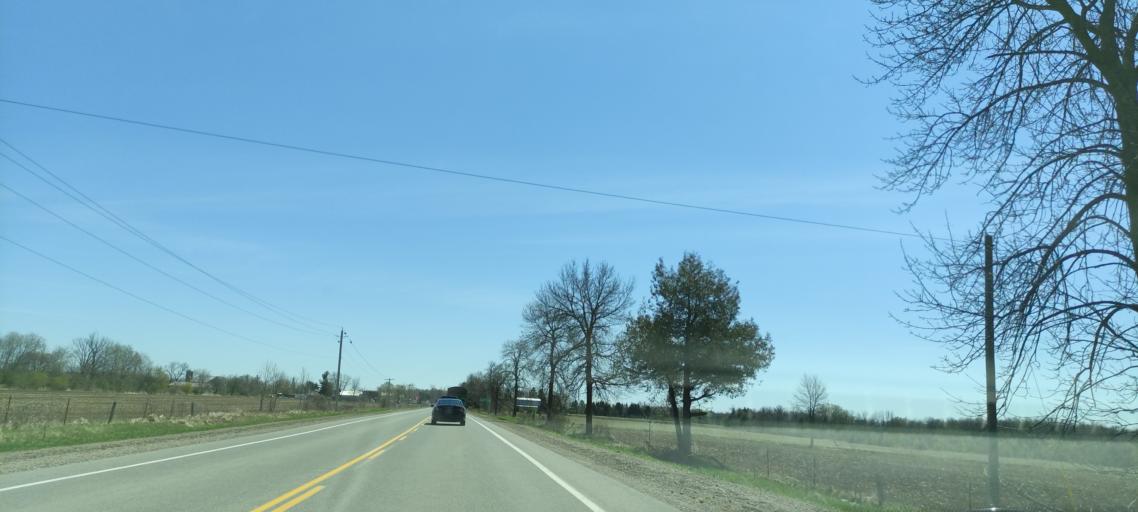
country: CA
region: Ontario
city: Waterloo
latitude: 43.5750
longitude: -80.4077
